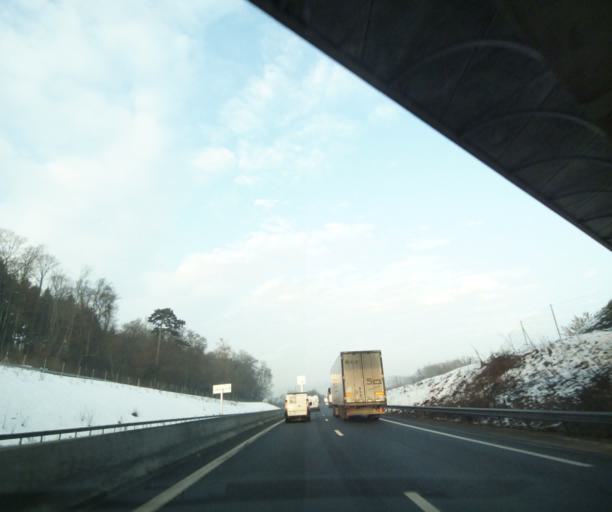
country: FR
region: Rhone-Alpes
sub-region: Departement de l'Isere
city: La Tour-du-Pin
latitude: 45.5598
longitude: 5.4453
